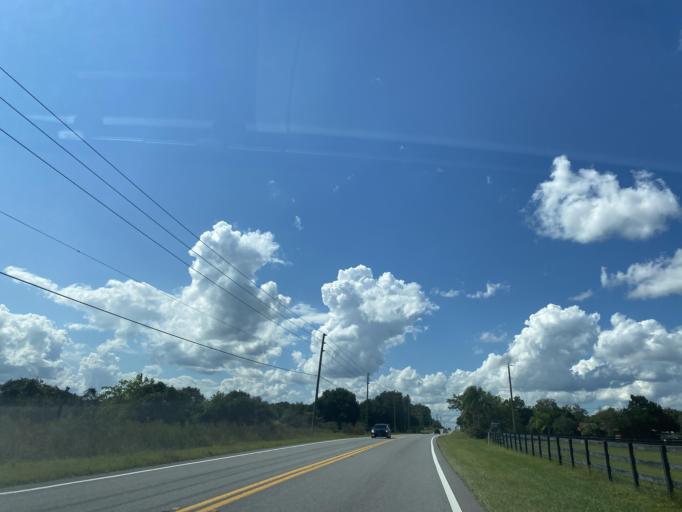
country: US
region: Florida
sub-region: Lake County
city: Lady Lake
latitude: 28.9800
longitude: -81.8742
